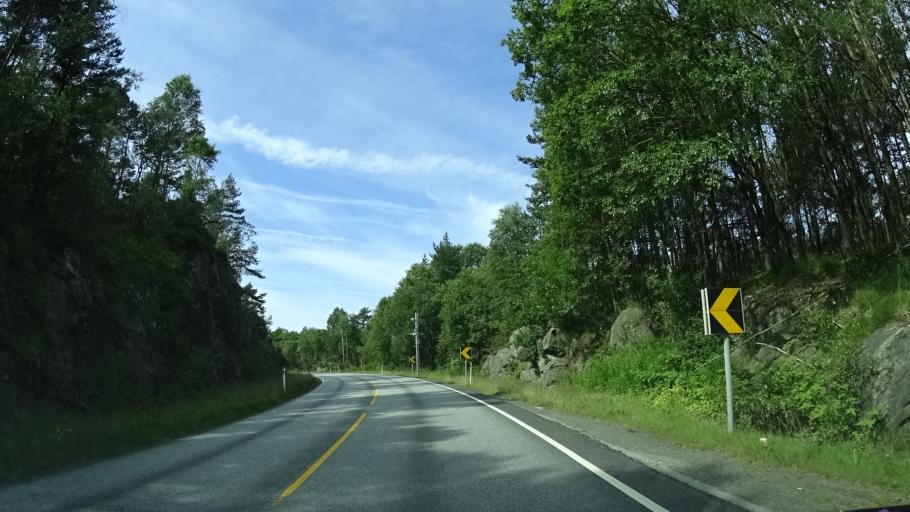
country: NO
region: Hordaland
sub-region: Bomlo
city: Mosterhamn
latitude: 59.6252
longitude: 5.4859
